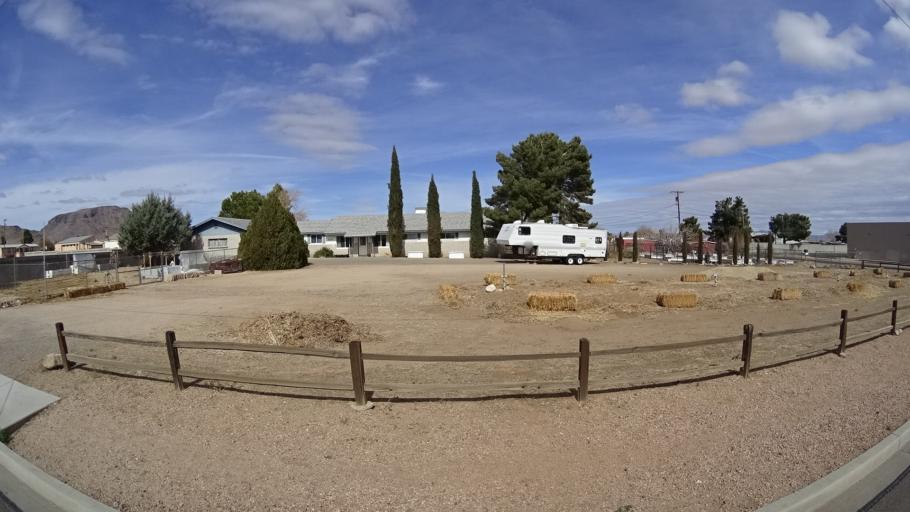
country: US
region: Arizona
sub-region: Mohave County
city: New Kingman-Butler
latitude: 35.2396
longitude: -114.0289
